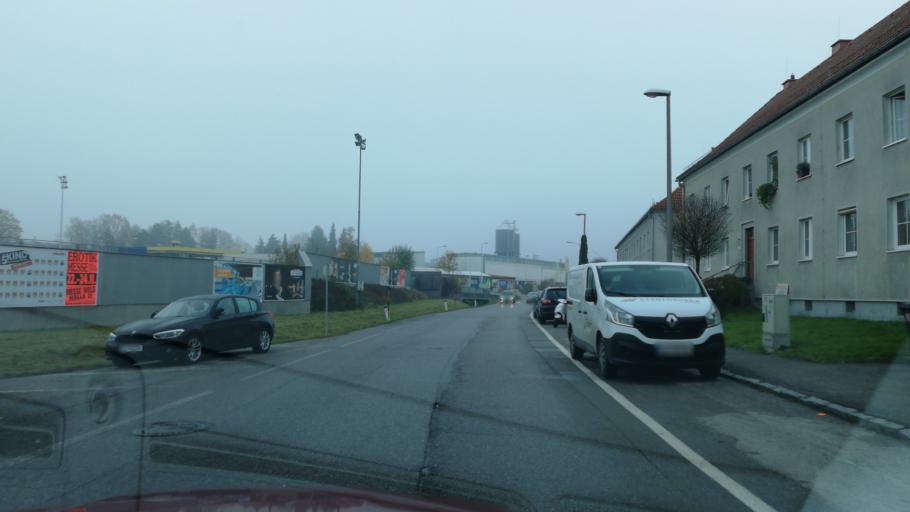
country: AT
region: Upper Austria
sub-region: Politischer Bezirk Ried im Innkreis
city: Ried im Innkreis
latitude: 48.2165
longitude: 13.4926
